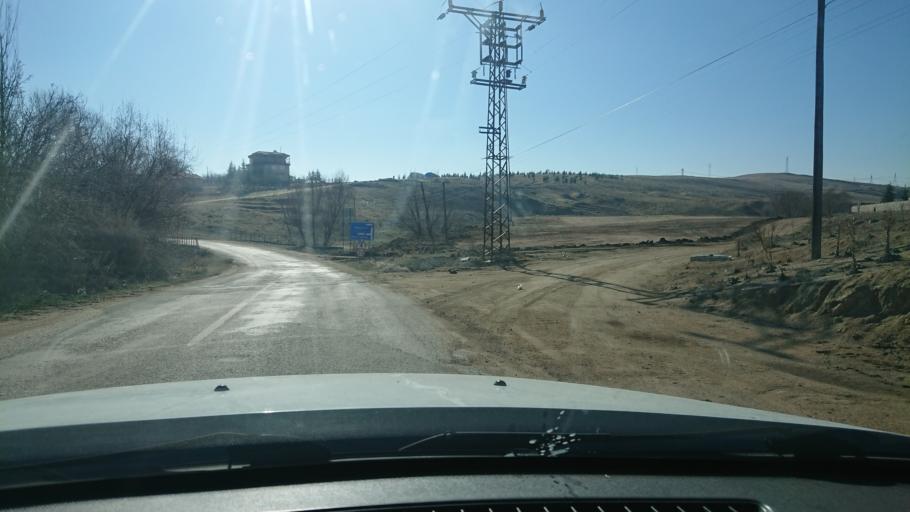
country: TR
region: Aksaray
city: Agacoren
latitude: 38.9200
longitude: 33.9274
